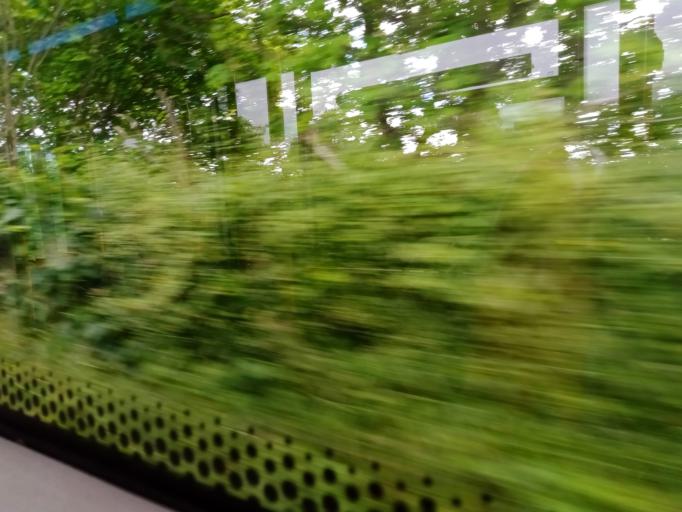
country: GB
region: Wales
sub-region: Anglesey
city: Llangoed
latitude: 53.2877
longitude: -4.0854
